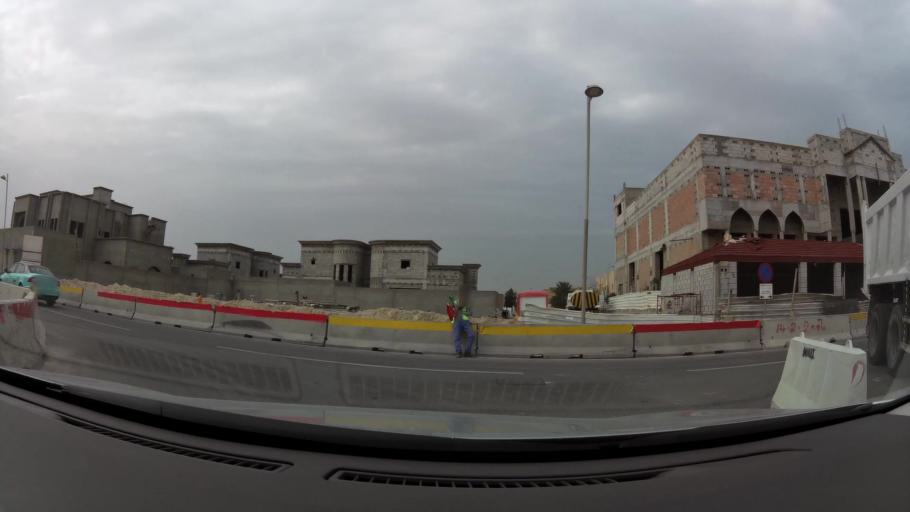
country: QA
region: Baladiyat ad Dawhah
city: Doha
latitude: 25.3443
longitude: 51.4868
